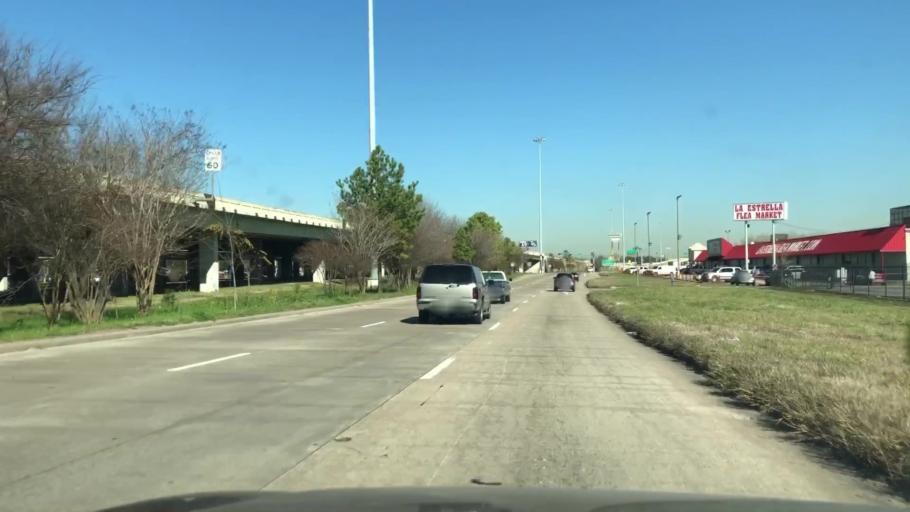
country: US
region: Texas
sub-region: Harris County
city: Aldine
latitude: 29.8621
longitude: -95.3328
